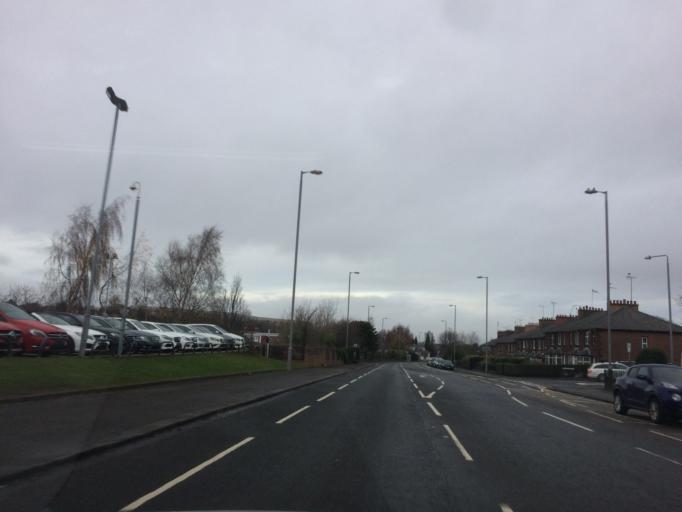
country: GB
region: Scotland
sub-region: East Renfrewshire
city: Giffnock
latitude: 55.8087
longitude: -4.2939
